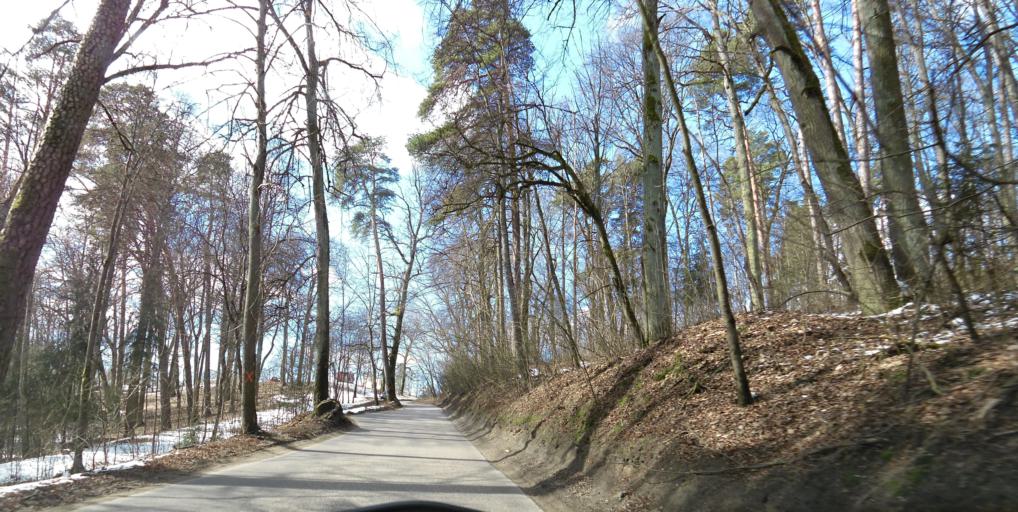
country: LT
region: Vilnius County
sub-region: Vilnius
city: Fabijoniskes
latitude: 54.7521
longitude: 25.2982
